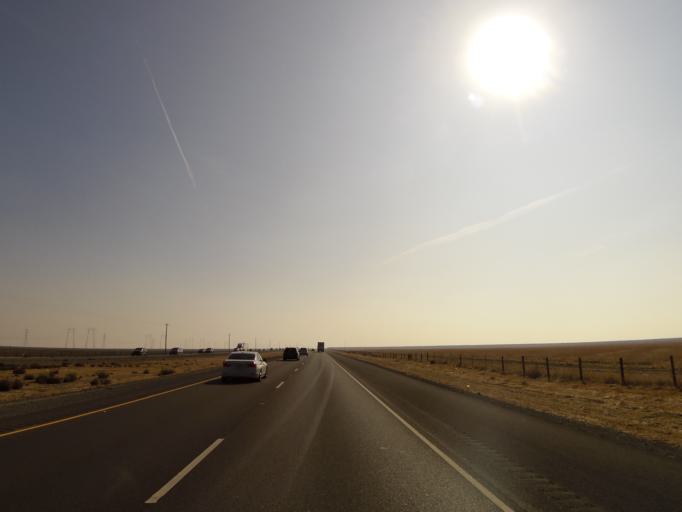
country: US
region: California
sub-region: Kings County
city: Kettleman City
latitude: 35.9010
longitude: -119.8780
